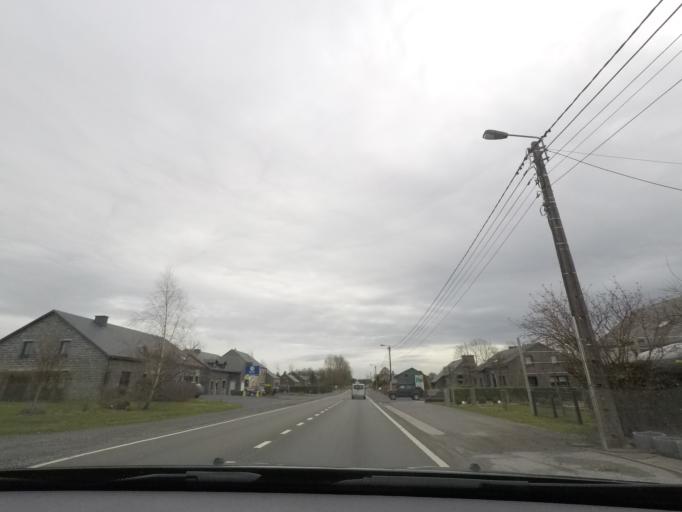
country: BE
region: Wallonia
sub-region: Province du Luxembourg
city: Bastogne
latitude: 49.9905
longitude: 5.7499
